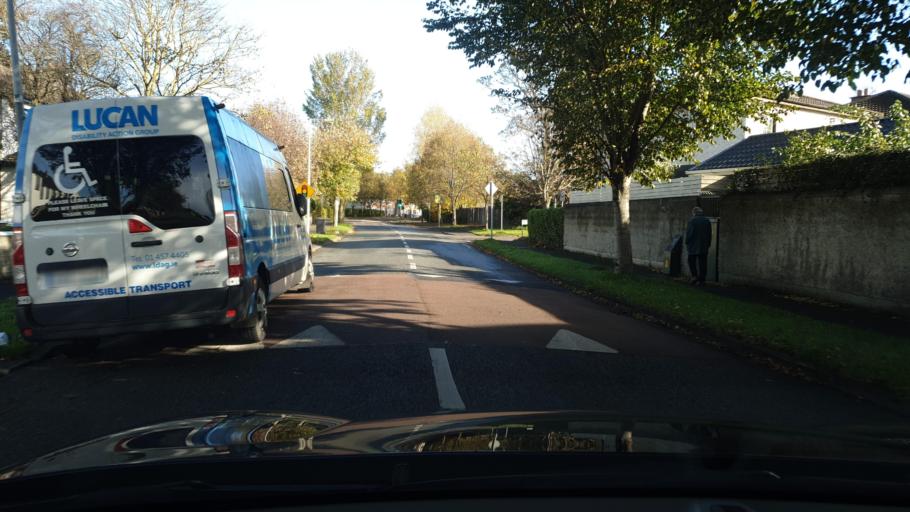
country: IE
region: Leinster
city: Lucan
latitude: 53.3503
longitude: -6.4397
